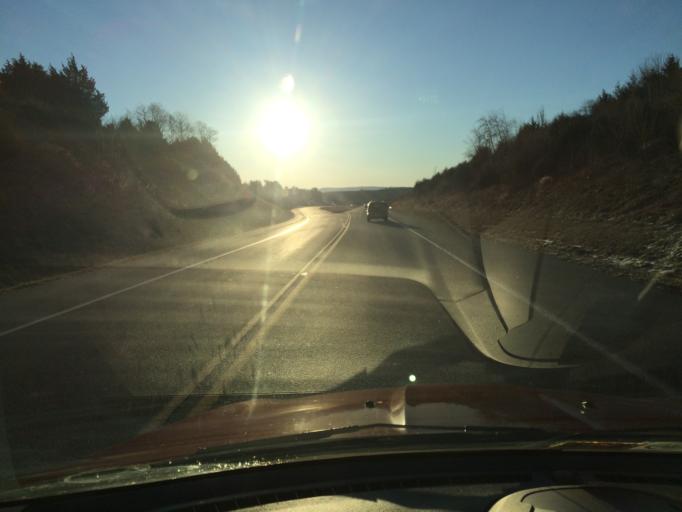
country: US
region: Virginia
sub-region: Augusta County
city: Verona
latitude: 38.1739
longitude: -79.0215
